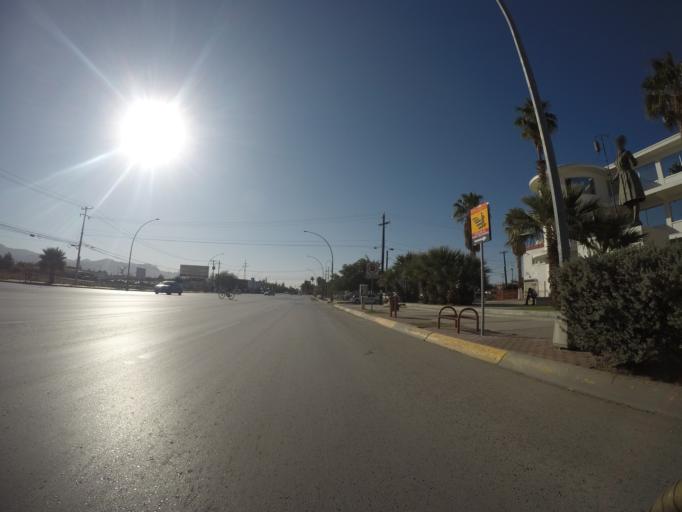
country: MX
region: Chihuahua
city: Ciudad Juarez
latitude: 31.7376
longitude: -106.4564
